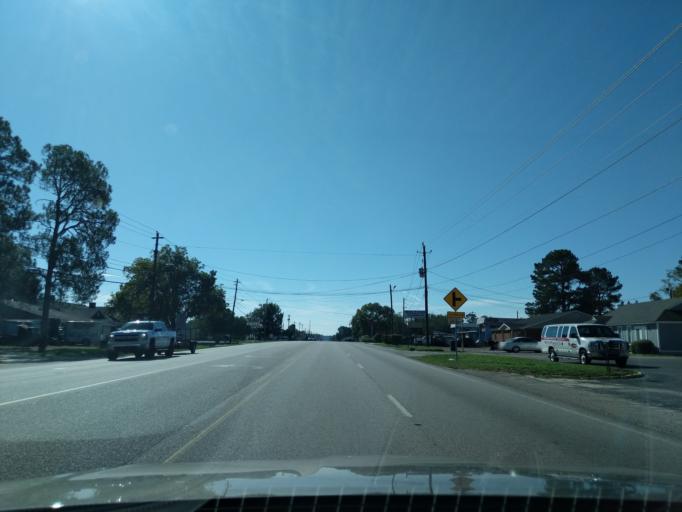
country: US
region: Georgia
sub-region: Richmond County
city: Augusta
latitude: 33.4162
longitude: -82.0070
